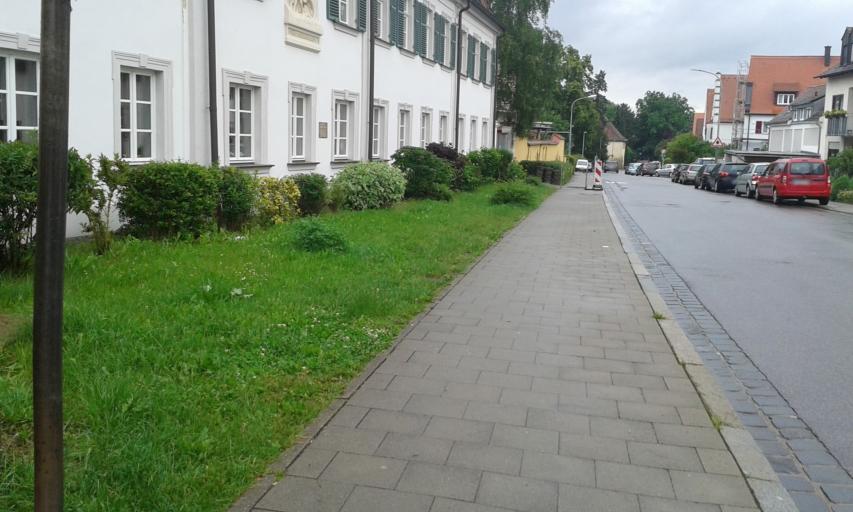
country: DE
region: Bavaria
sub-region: Upper Franconia
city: Bamberg
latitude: 49.8819
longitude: 10.8861
